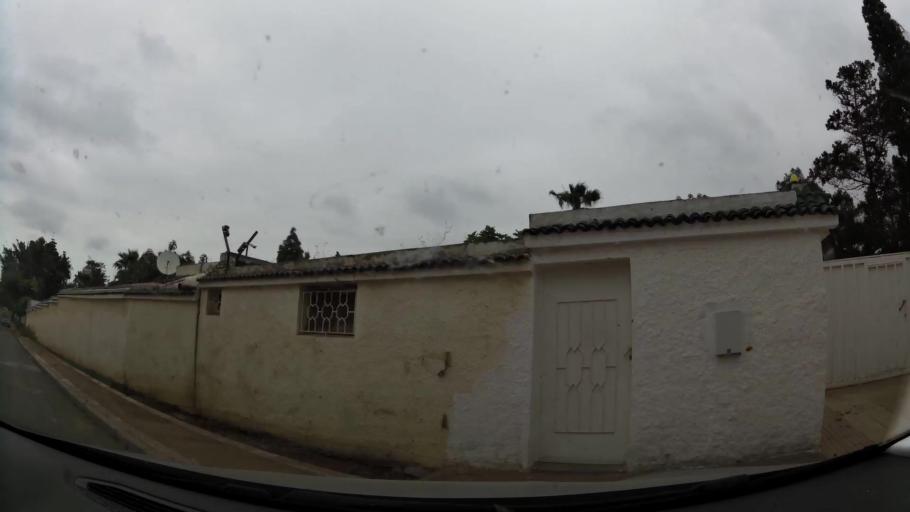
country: MA
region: Rabat-Sale-Zemmour-Zaer
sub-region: Rabat
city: Rabat
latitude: 33.9566
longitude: -6.8153
